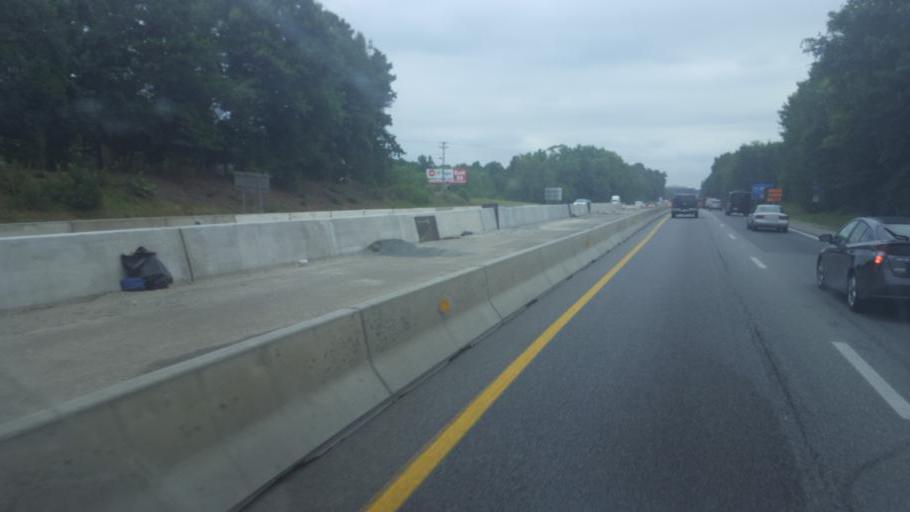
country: US
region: North Carolina
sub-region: Mecklenburg County
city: Cornelius
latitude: 35.4888
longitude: -80.8733
